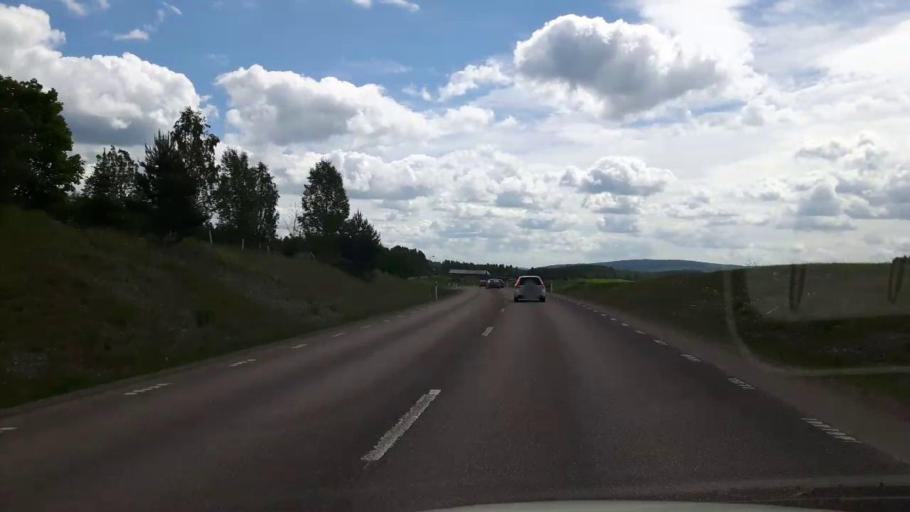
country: SE
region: Dalarna
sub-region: Saters Kommun
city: Saeter
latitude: 60.4425
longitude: 15.8123
